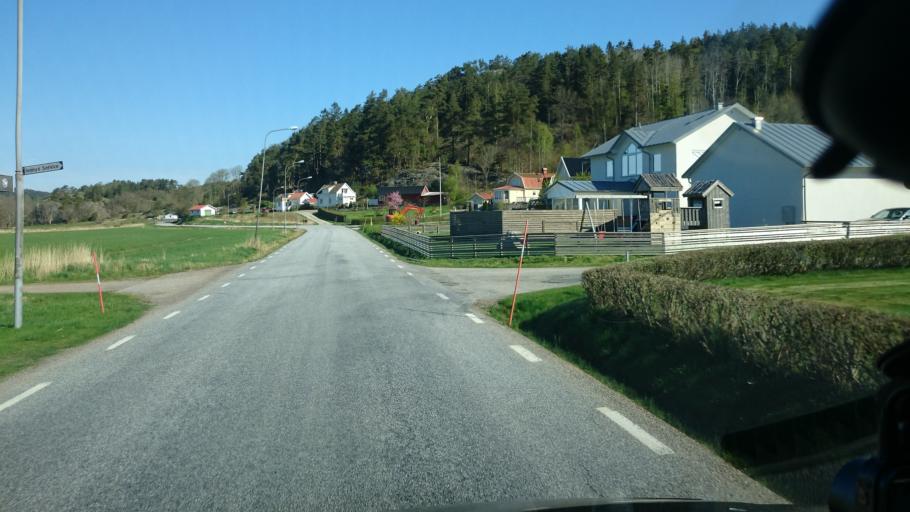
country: SE
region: Vaestra Goetaland
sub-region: Munkedals Kommun
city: Munkedal
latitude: 58.3814
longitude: 11.6663
